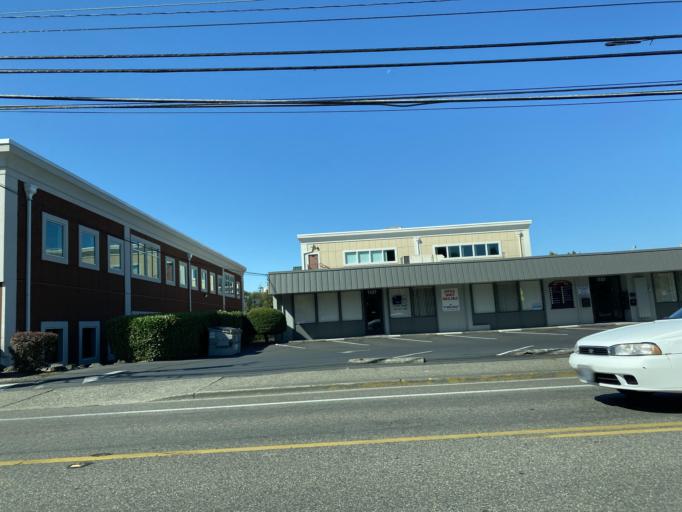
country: US
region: Washington
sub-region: Thurston County
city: Olympia
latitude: 47.0386
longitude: -122.8874
